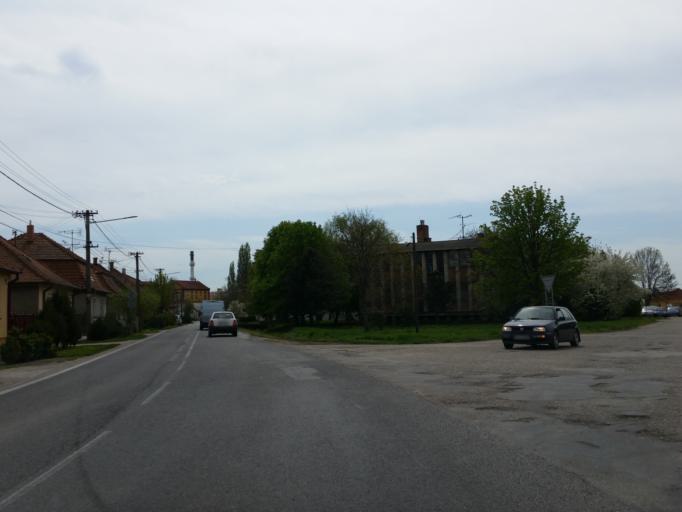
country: SK
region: Trnavsky
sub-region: Okres Dunajska Streda
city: Velky Meder
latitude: 47.8609
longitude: 17.7764
